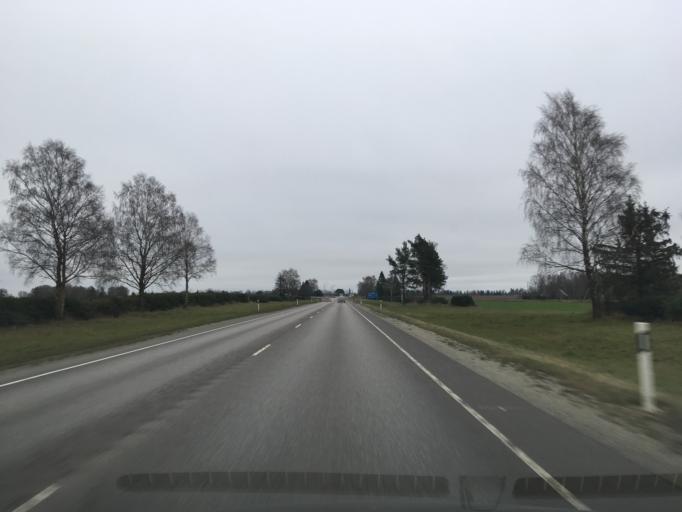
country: EE
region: Laeaene-Virumaa
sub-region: Haljala vald
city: Haljala
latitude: 59.4174
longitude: 26.3283
